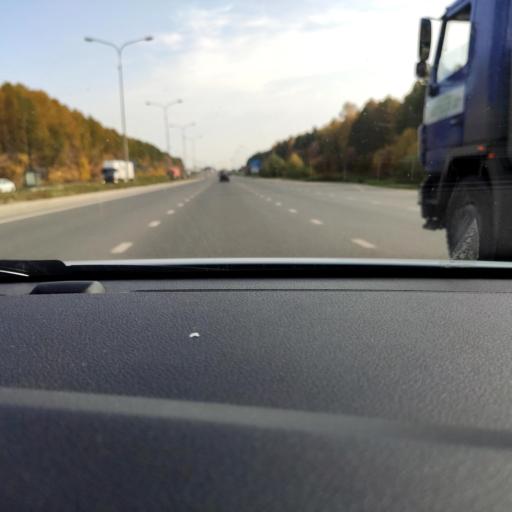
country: RU
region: Tatarstan
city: Vysokaya Gora
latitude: 55.8014
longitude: 49.3256
